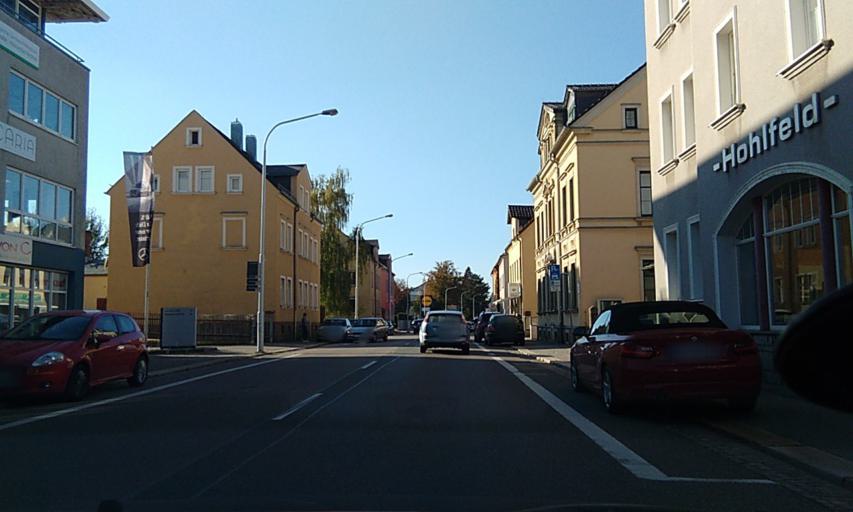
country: DE
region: Saxony
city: Limbach-Oberfrohna
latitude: 50.8546
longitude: 12.7806
